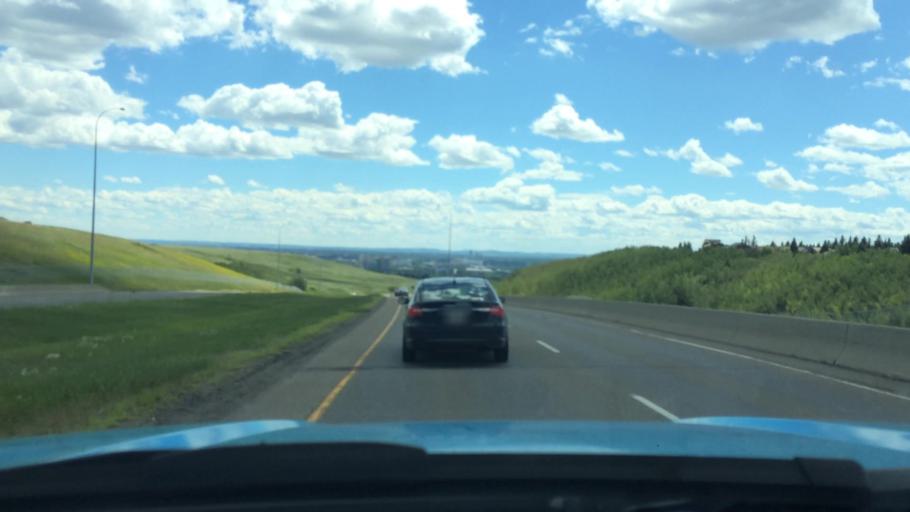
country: CA
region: Alberta
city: Calgary
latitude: 51.1228
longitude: -114.1346
